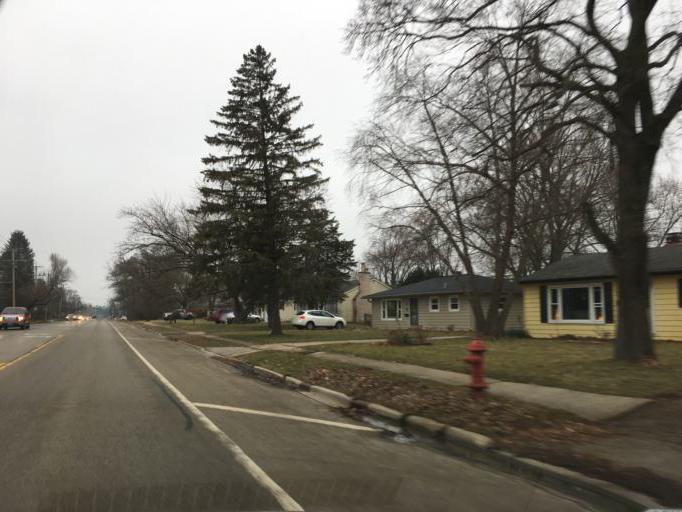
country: US
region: Illinois
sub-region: McHenry County
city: Lakewood
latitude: 42.2246
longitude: -88.3375
